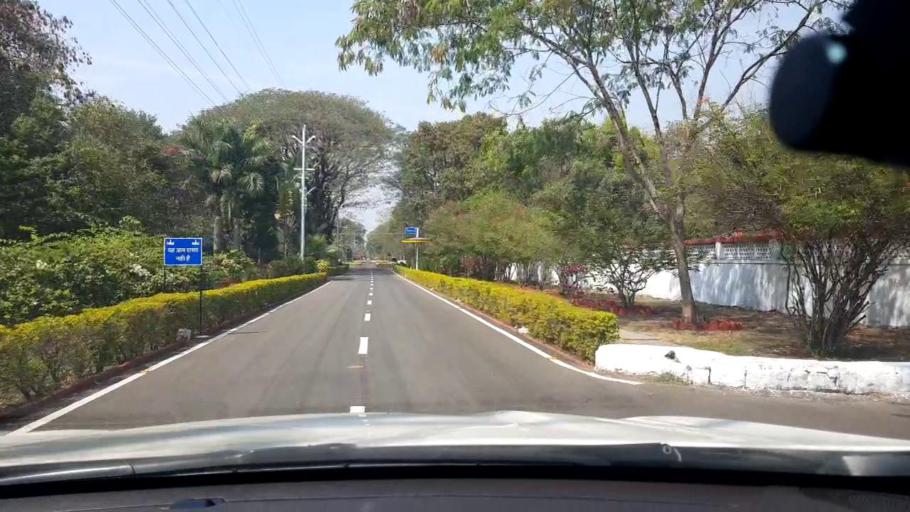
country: IN
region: Maharashtra
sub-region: Pune Division
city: Shivaji Nagar
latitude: 18.5447
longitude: 73.8647
